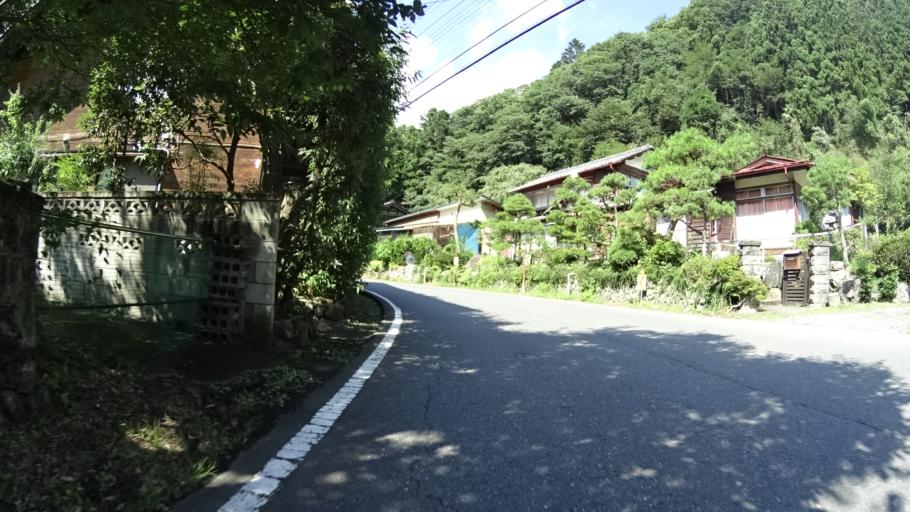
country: JP
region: Saitama
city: Chichibu
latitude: 36.0390
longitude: 138.9076
